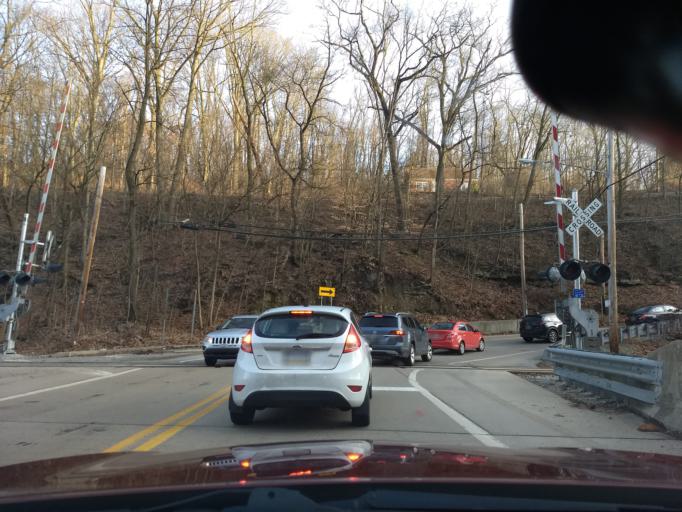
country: US
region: Pennsylvania
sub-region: Allegheny County
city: Pleasant Hills
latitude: 40.3569
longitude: -79.9558
